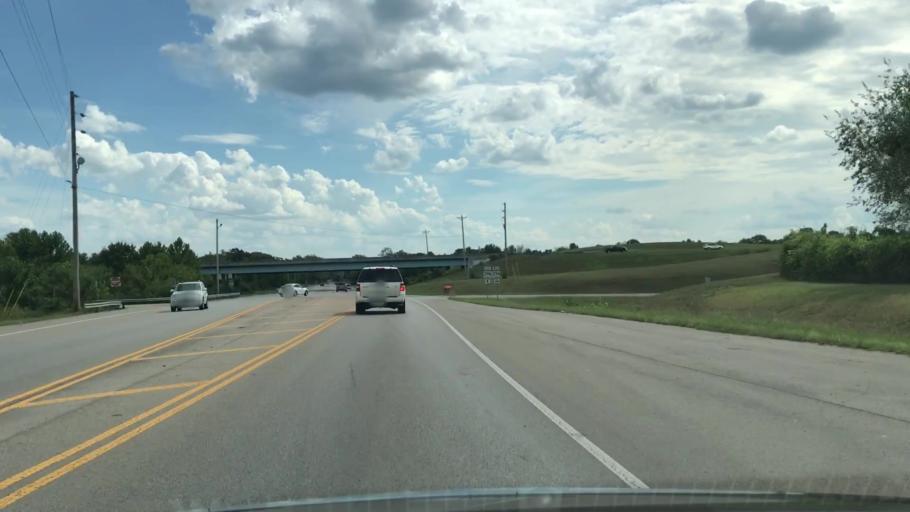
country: US
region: Tennessee
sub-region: Maury County
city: Spring Hill
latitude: 35.7347
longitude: -86.9247
